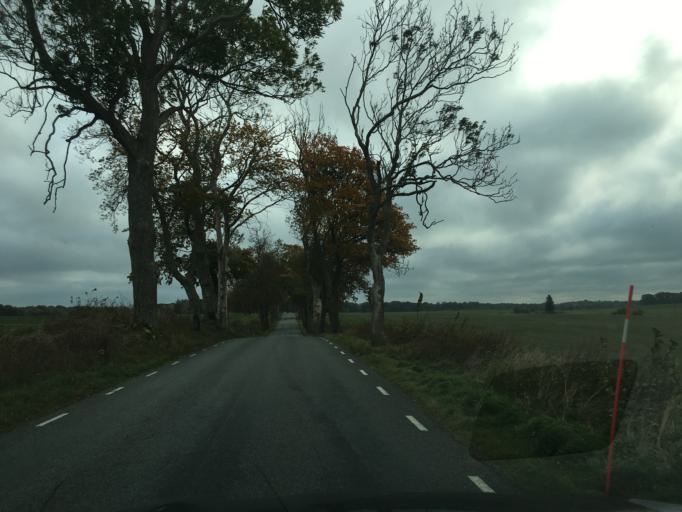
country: SE
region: Skane
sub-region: Tomelilla Kommun
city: Tomelilla
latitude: 55.6504
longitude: 14.0345
